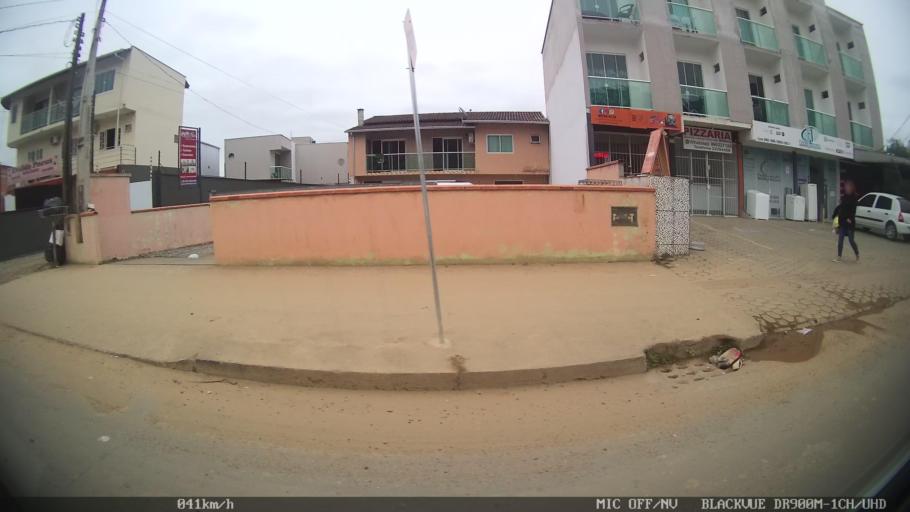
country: BR
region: Santa Catarina
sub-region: Joinville
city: Joinville
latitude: -26.3628
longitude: -48.8241
